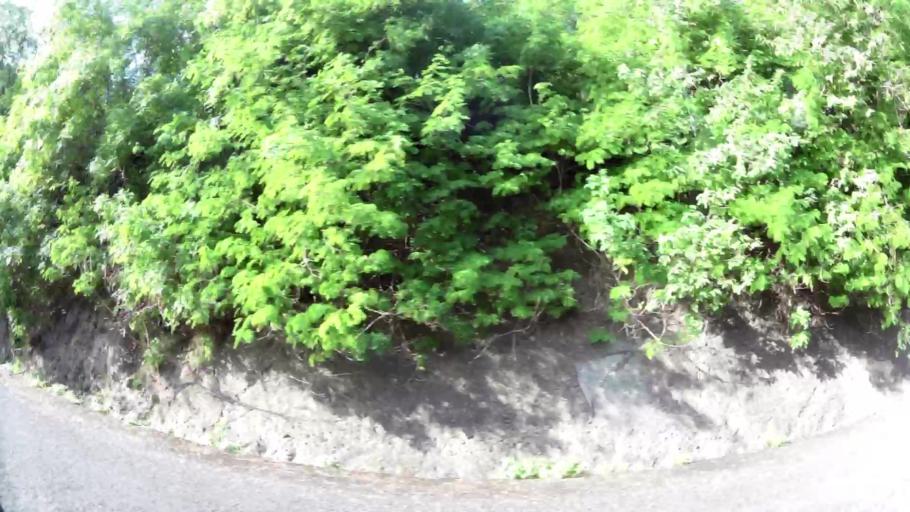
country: LC
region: Anse-la-Raye
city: Canaries
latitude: 13.9026
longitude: -61.0682
